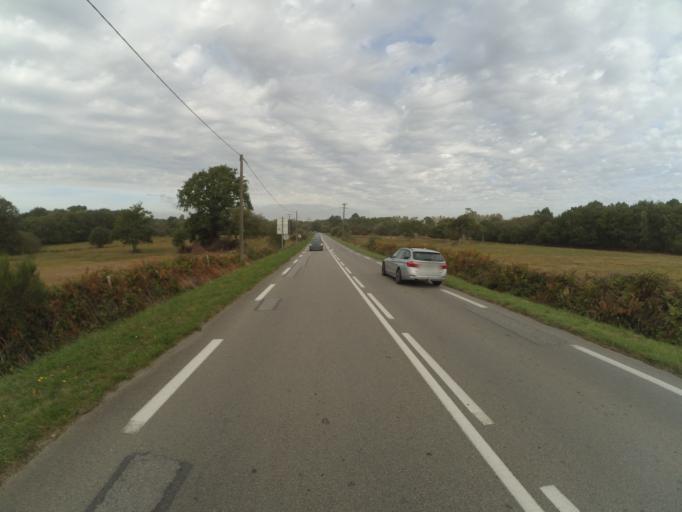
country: FR
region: Brittany
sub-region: Departement du Morbihan
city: Sainte-Helene
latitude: 47.7139
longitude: -3.2240
